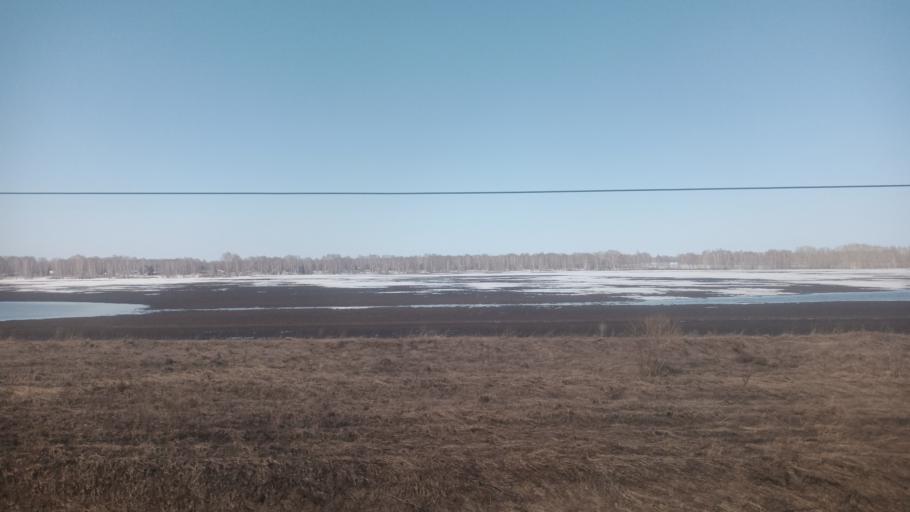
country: RU
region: Altai Krai
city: Logovskoye
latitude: 53.4826
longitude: 84.1391
